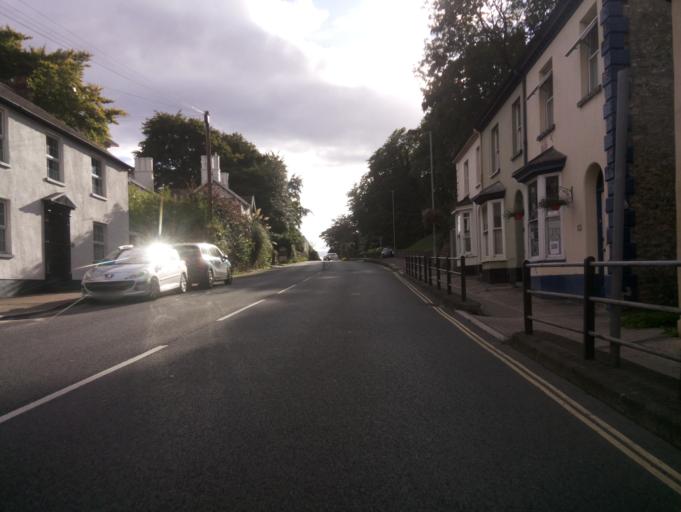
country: GB
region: England
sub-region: Devon
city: Honiton
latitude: 50.7979
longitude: -3.1954
